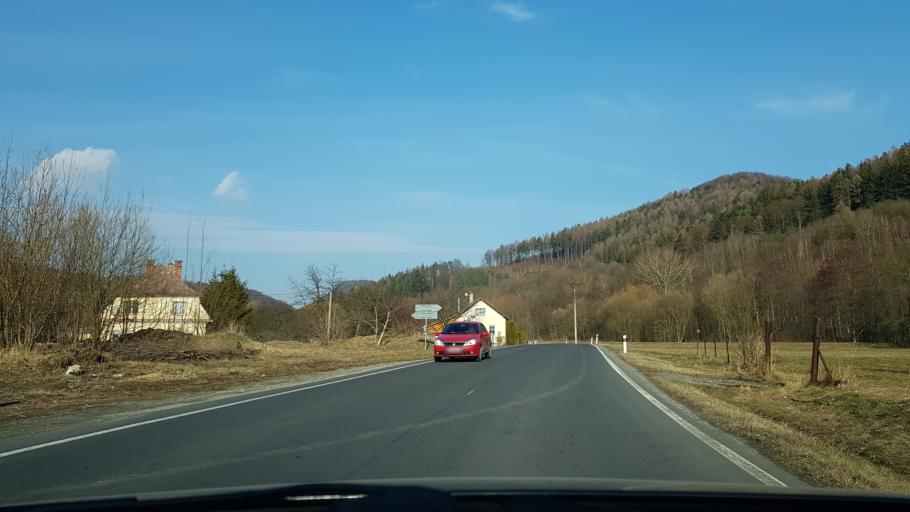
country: CZ
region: Olomoucky
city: Dolni Bohdikov
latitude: 50.0312
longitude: 16.9032
